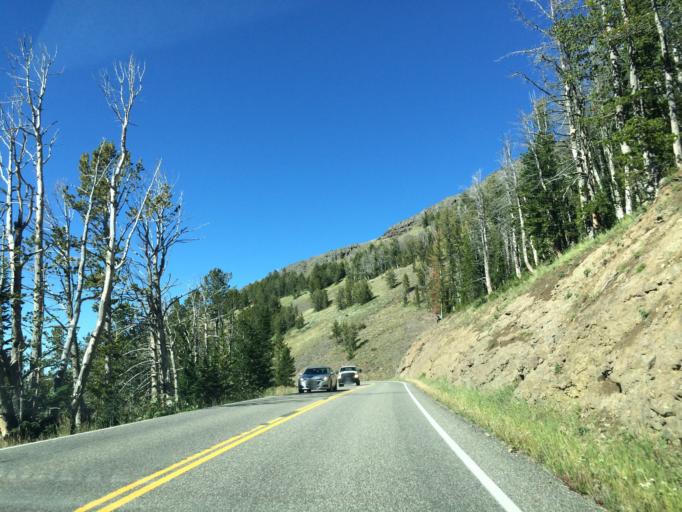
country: US
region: Montana
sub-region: Gallatin County
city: West Yellowstone
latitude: 44.7995
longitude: -110.4455
